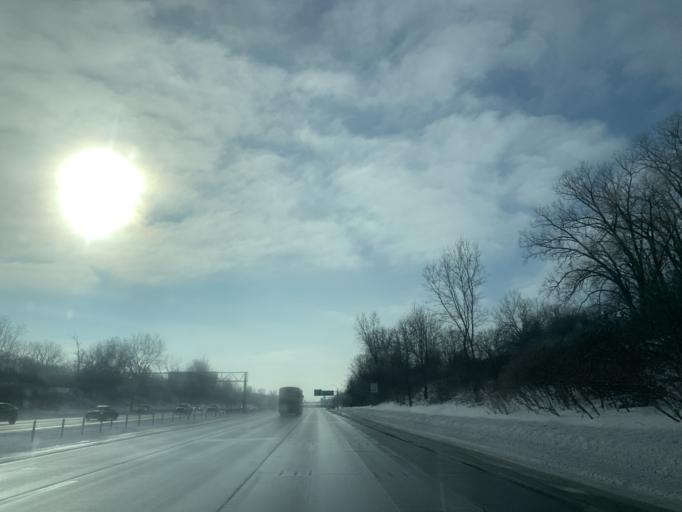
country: US
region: Minnesota
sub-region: Dakota County
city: Apple Valley
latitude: 44.7719
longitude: -93.2176
